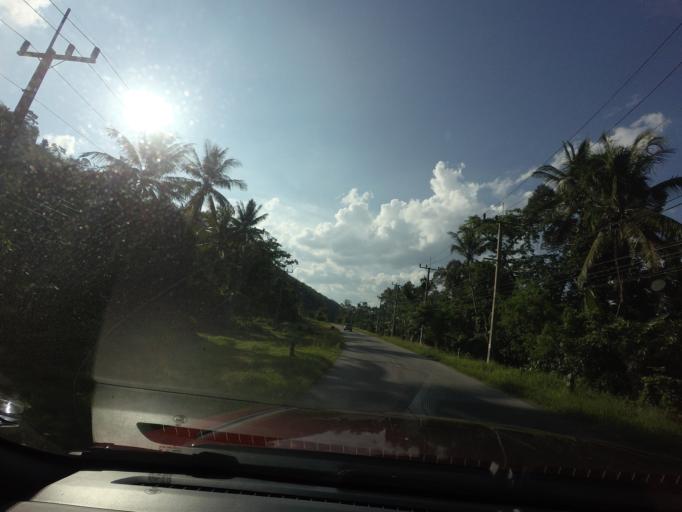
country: TH
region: Yala
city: Than To
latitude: 6.1701
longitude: 101.2679
